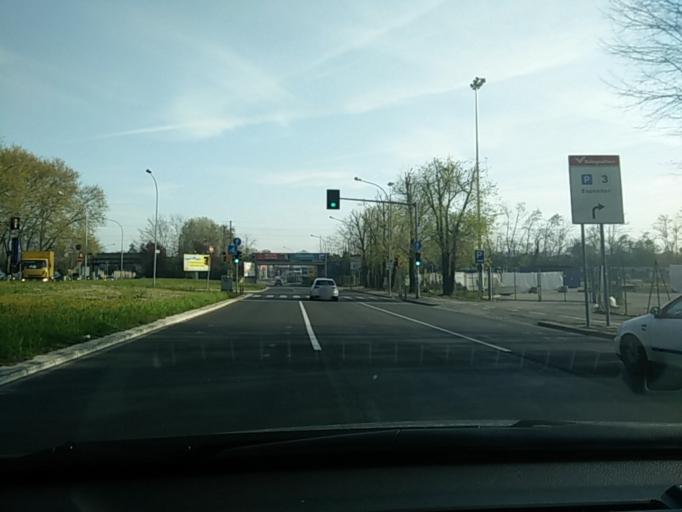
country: IT
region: Emilia-Romagna
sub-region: Provincia di Bologna
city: Bologna
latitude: 44.5169
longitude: 11.3602
